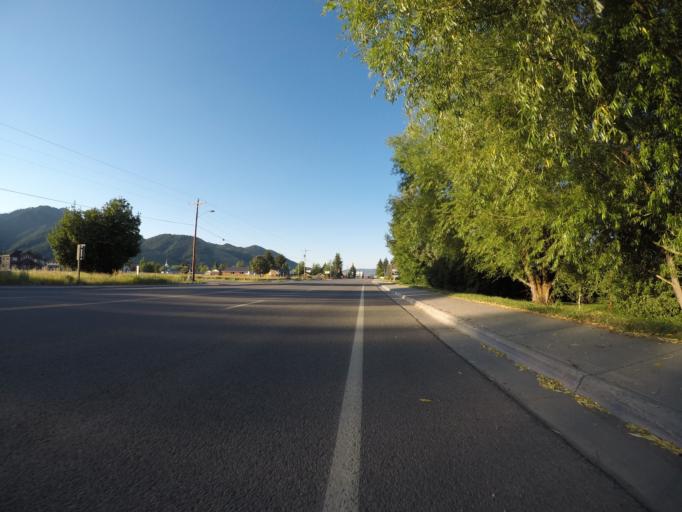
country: US
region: Wyoming
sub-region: Lincoln County
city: Afton
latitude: 42.7320
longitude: -110.9334
